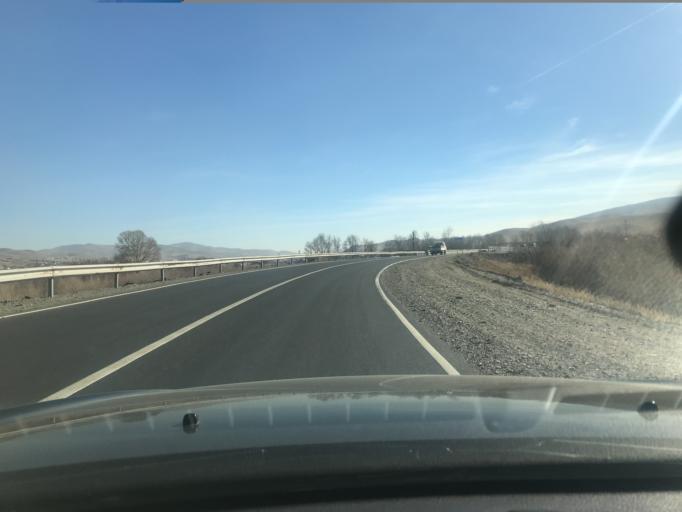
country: MN
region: Ulaanbaatar
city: Ulaanbaatar
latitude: 47.8960
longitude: 107.0632
